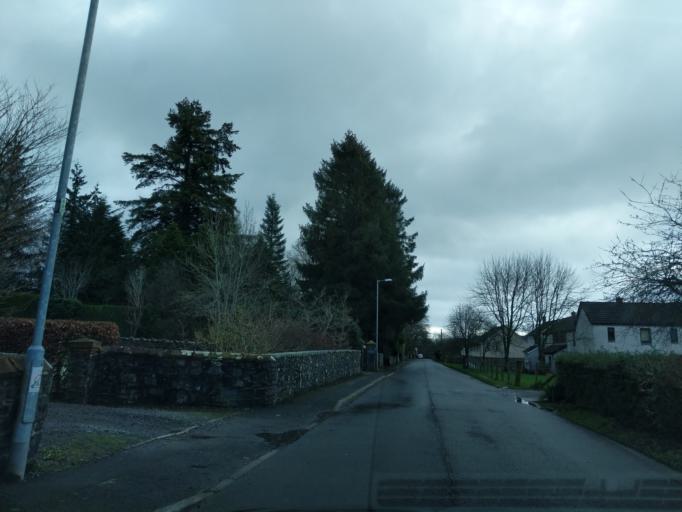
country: GB
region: Scotland
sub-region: Dumfries and Galloway
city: Moffat
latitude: 55.3335
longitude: -3.4325
